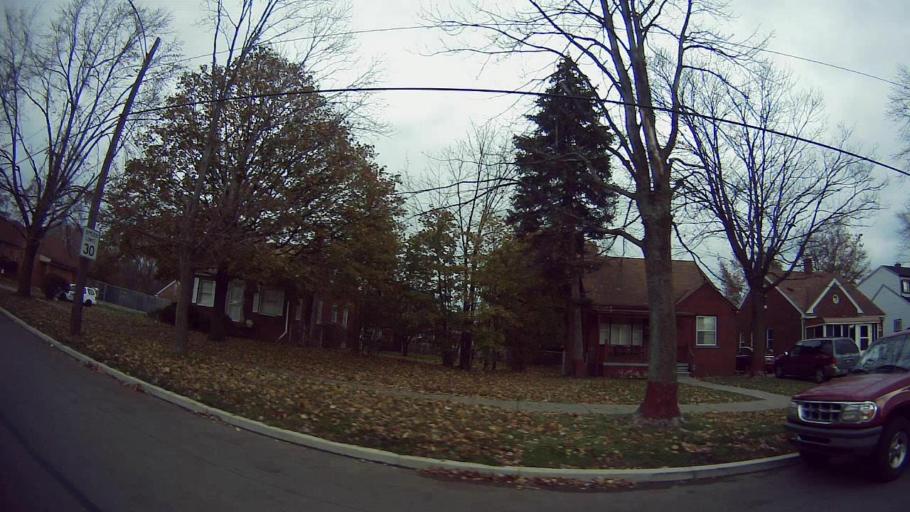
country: US
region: Michigan
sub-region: Macomb County
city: Eastpointe
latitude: 42.4383
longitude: -82.9852
